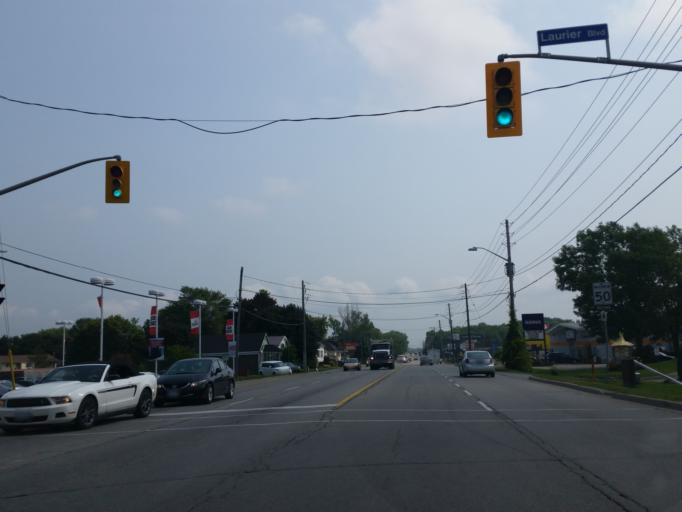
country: CA
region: Ontario
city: Brockville
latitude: 44.6042
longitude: -75.7152
